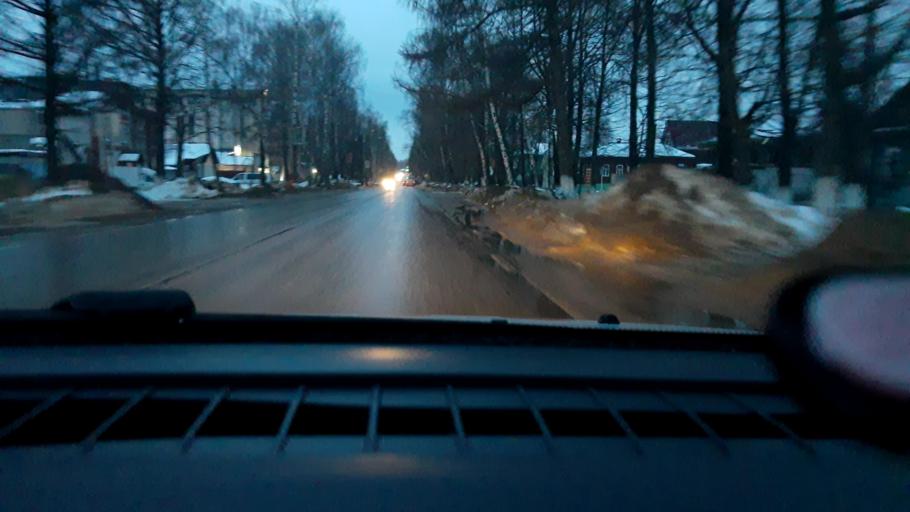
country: RU
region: Nizjnij Novgorod
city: Lyskovo
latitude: 56.0387
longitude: 45.0461
